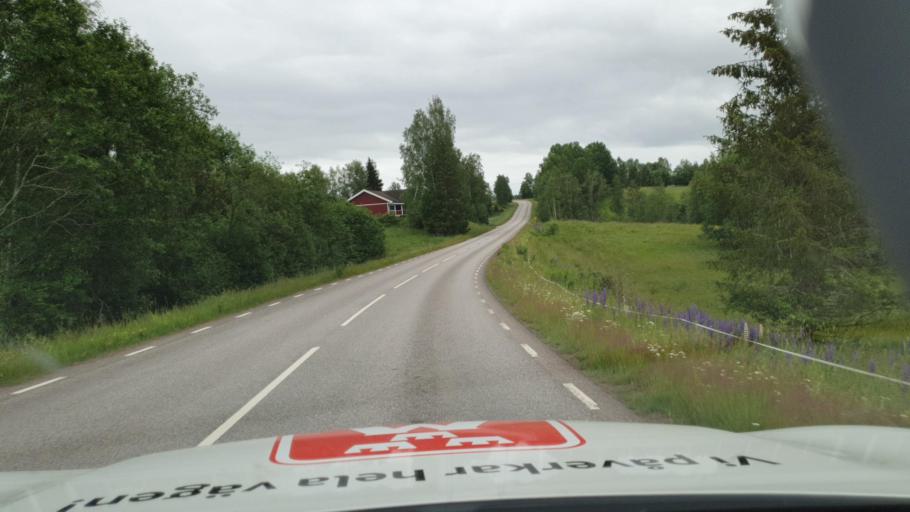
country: SE
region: Vaermland
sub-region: Sunne Kommun
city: Sunne
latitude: 59.7921
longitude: 13.0779
